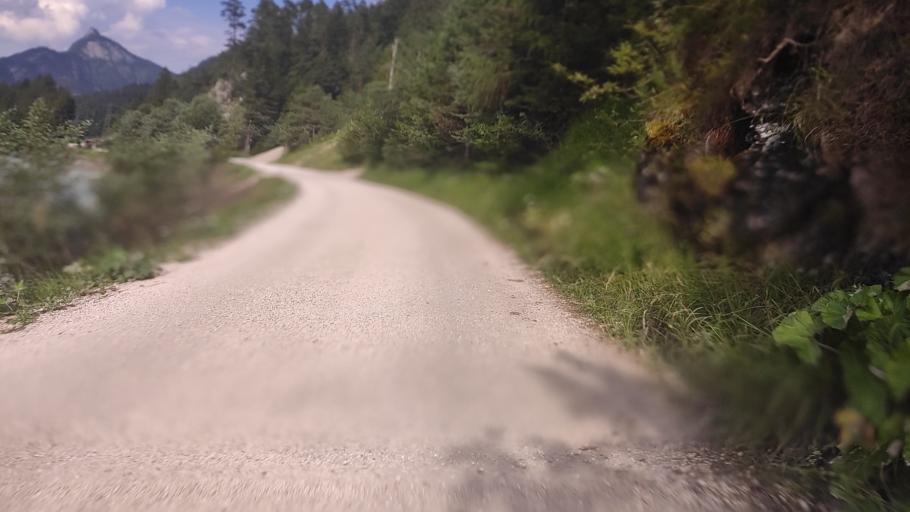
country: DE
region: Bavaria
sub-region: Upper Bavaria
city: Schneizlreuth
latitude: 47.6654
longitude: 12.7720
